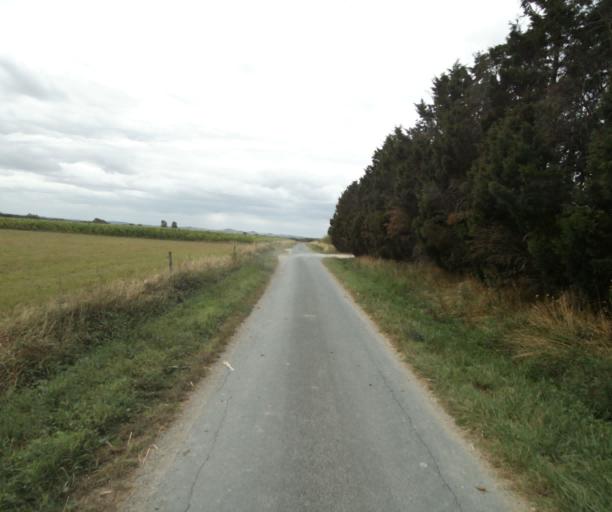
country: FR
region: Midi-Pyrenees
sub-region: Departement du Tarn
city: Soreze
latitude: 43.4709
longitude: 2.0567
